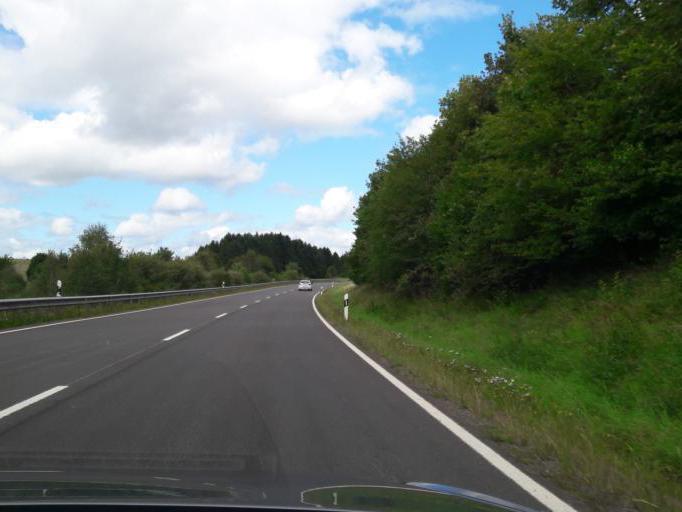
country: DE
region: Rheinland-Pfalz
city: Ruschberg
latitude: 49.6070
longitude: 7.3056
